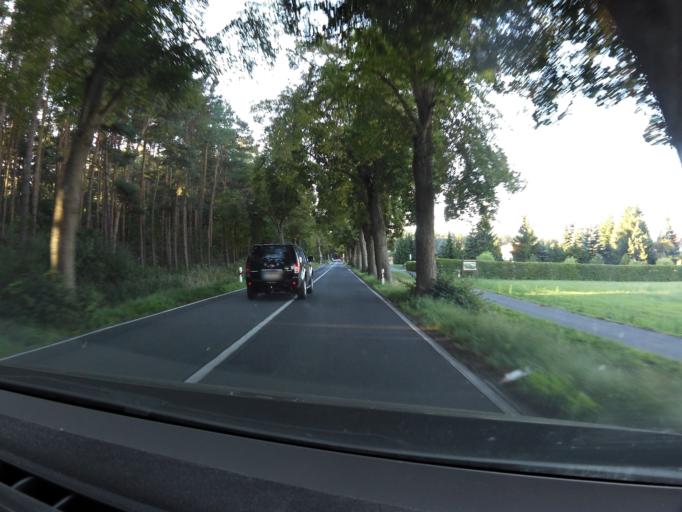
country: DE
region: Mecklenburg-Vorpommern
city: Usedom
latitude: 53.9129
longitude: 14.0189
